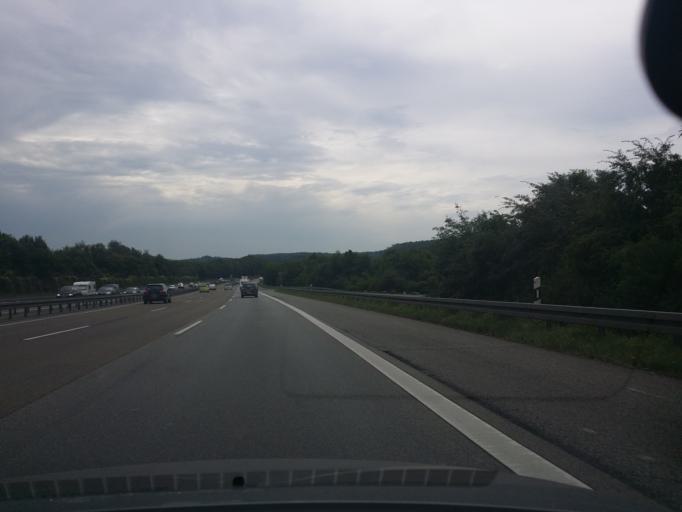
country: DE
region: Hesse
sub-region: Regierungsbezirk Darmstadt
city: Niedernhausen
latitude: 50.1634
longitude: 8.2980
